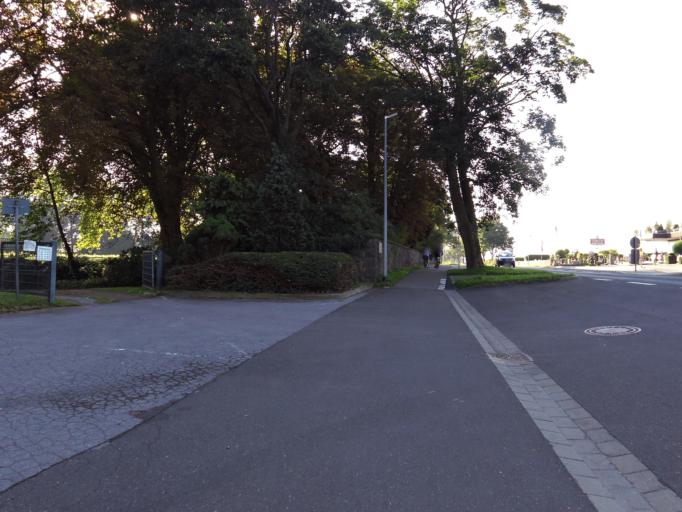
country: DE
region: North Rhine-Westphalia
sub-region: Regierungsbezirk Koln
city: Alsdorf
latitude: 50.8879
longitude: 6.1477
